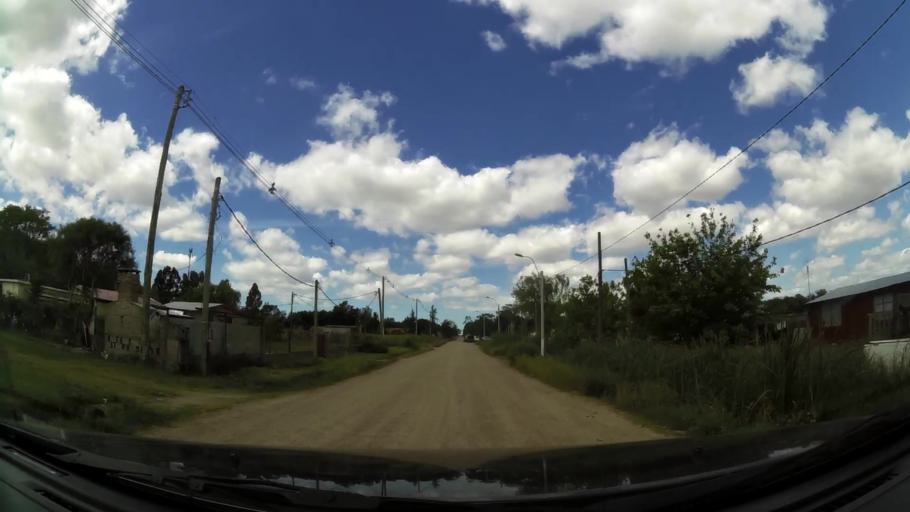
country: UY
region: Canelones
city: Colonia Nicolich
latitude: -34.8101
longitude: -56.0439
